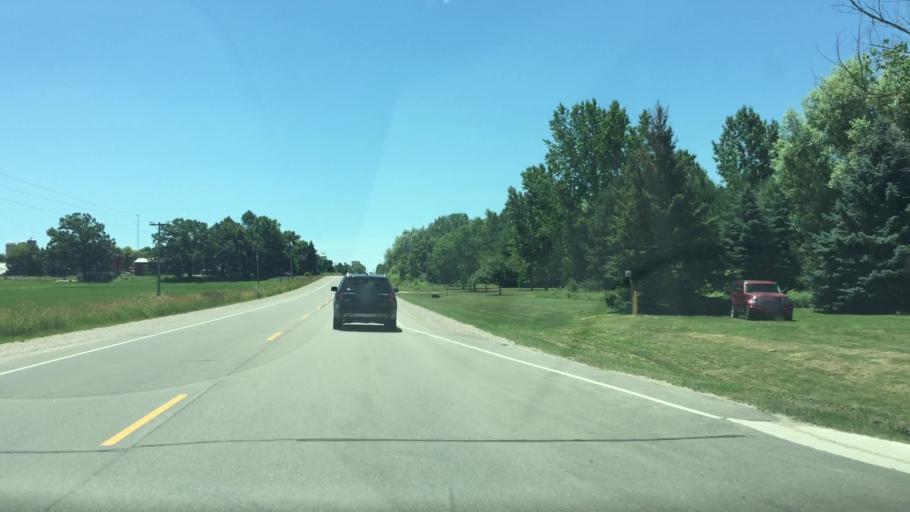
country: US
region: Wisconsin
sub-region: Calumet County
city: New Holstein
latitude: 43.9714
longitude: -88.1124
